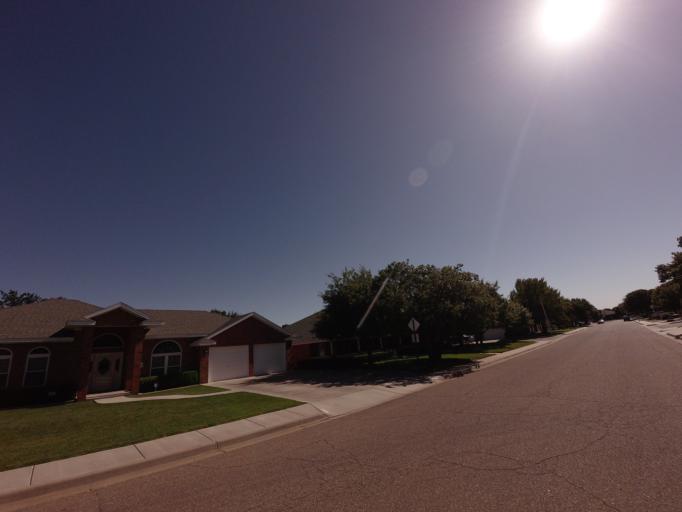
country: US
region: New Mexico
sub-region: Curry County
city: Clovis
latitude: 34.4250
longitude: -103.1728
